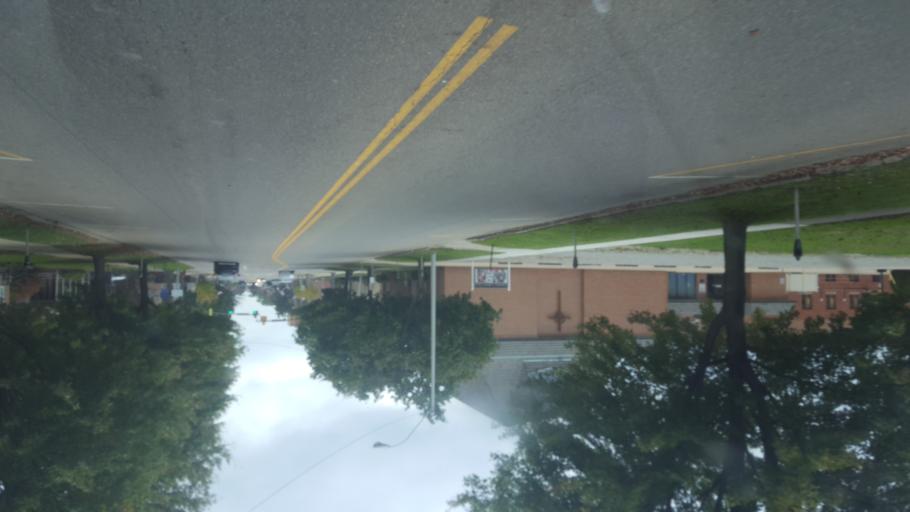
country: US
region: Ohio
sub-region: Tuscarawas County
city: New Philadelphia
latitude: 40.4891
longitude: -81.4423
